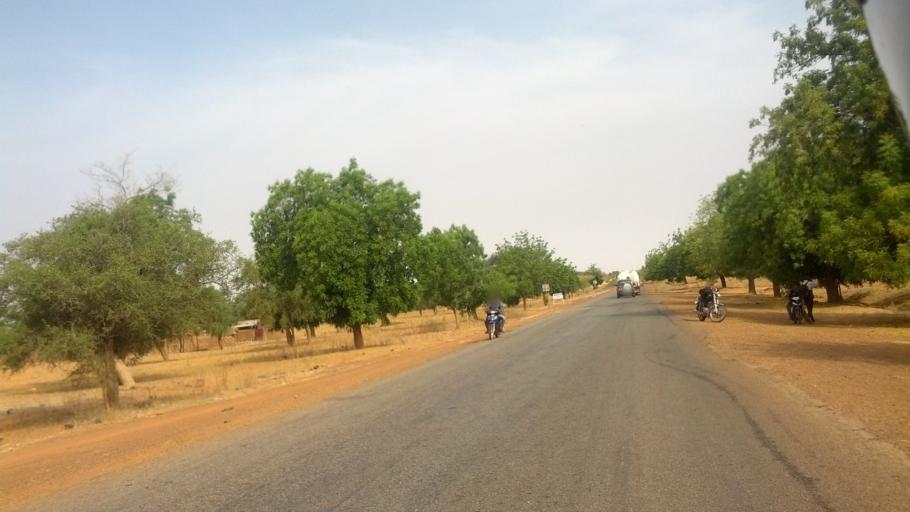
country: BF
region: Centre-Nord
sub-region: Province du Sanmatenga
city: Kaya
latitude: 12.9146
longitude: -1.0780
